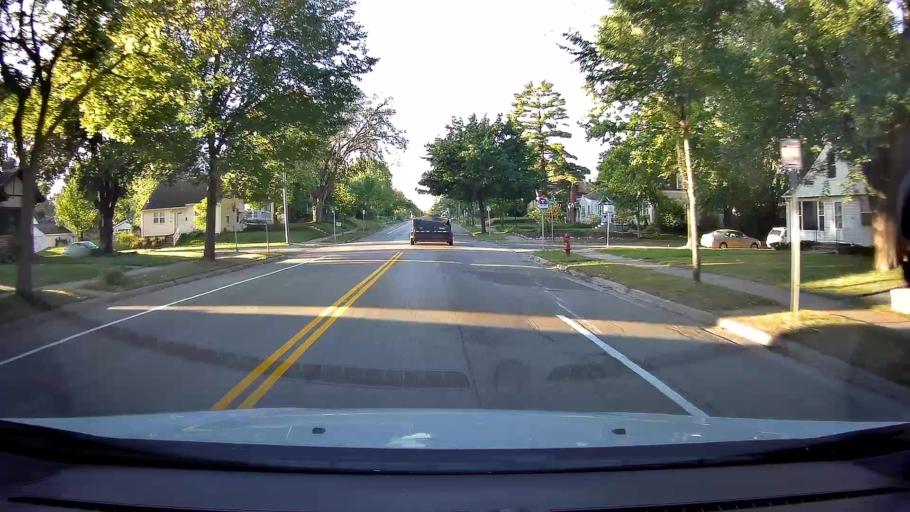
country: US
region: Minnesota
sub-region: Hennepin County
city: Richfield
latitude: 44.9218
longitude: -93.2473
